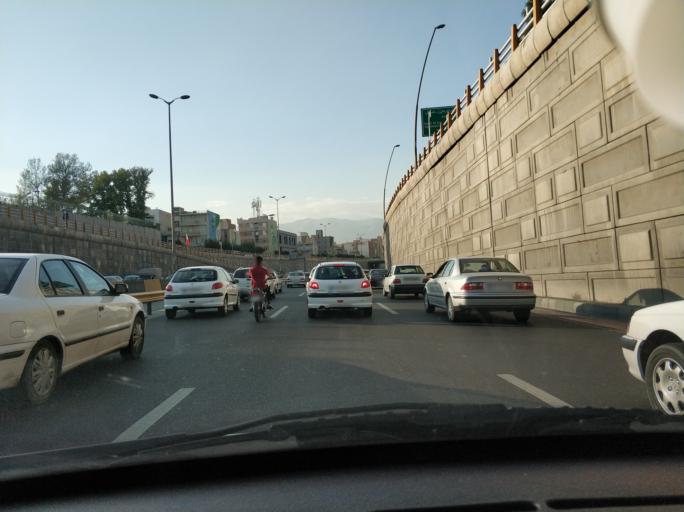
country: IR
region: Tehran
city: Tehran
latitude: 35.6941
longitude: 51.4568
